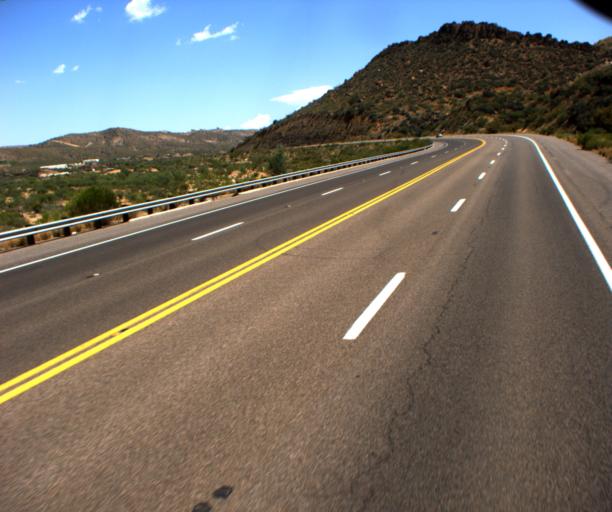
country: US
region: Arizona
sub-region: Gila County
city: Claypool
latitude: 33.4555
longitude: -110.8440
